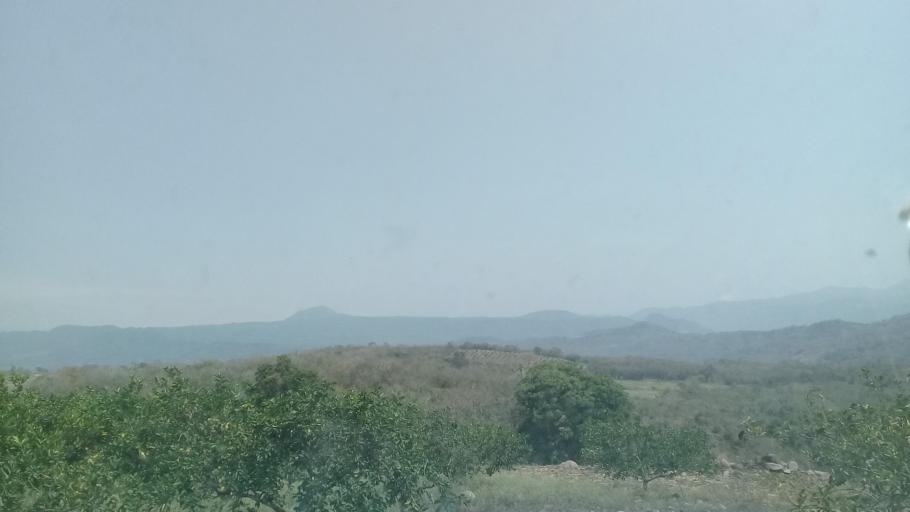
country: MX
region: Veracruz
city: El Castillo
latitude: 19.5703
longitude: -96.8060
